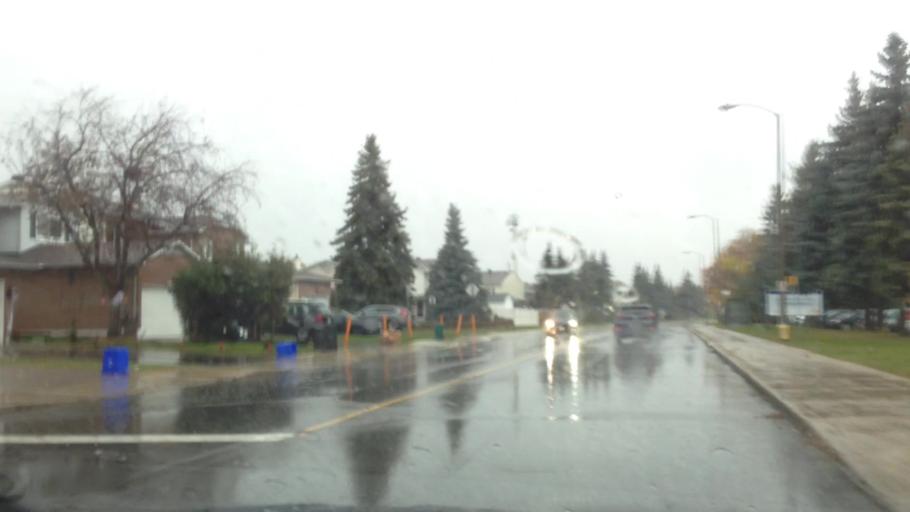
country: CA
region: Ontario
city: Clarence-Rockland
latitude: 45.4649
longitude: -75.4861
